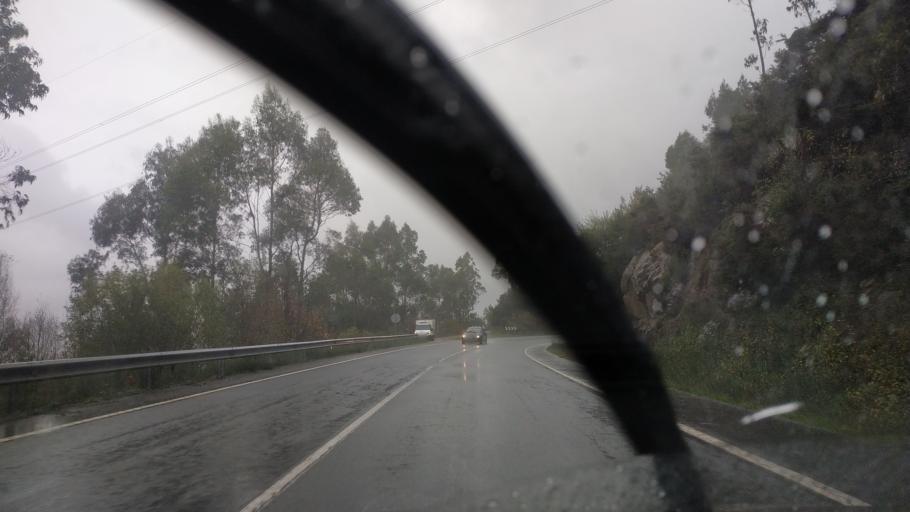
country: ES
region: Galicia
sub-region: Provincia da Coruna
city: Cerceda
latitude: 43.1705
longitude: -8.5095
